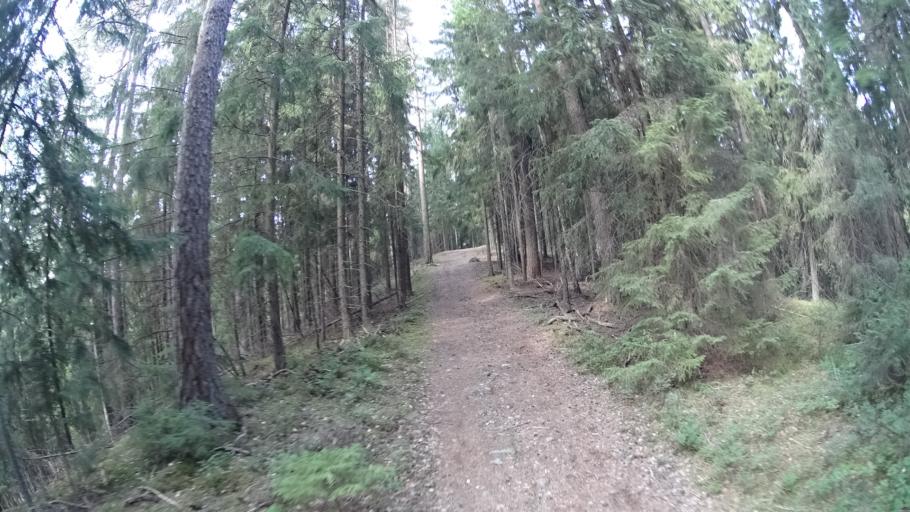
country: FI
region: Haeme
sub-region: Forssa
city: Tammela
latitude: 60.7754
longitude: 23.8390
